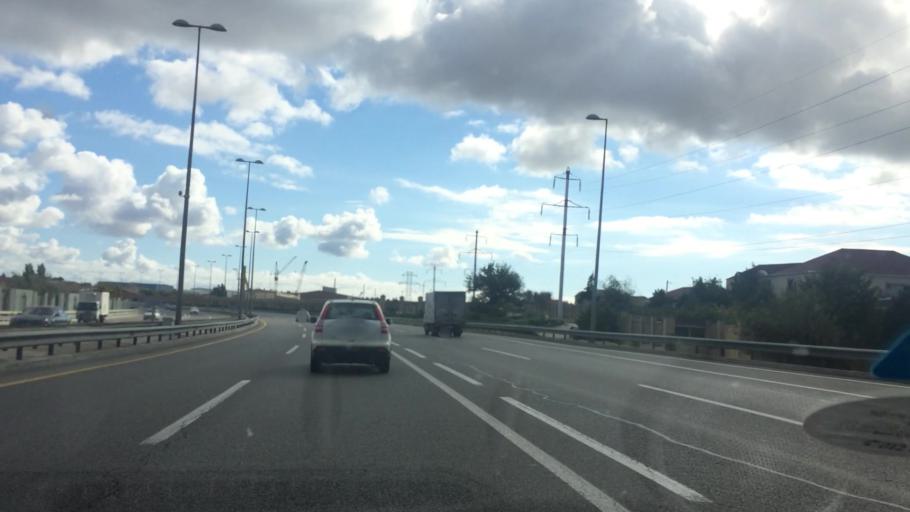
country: AZ
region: Baki
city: Ramana
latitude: 40.4388
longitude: 49.9747
